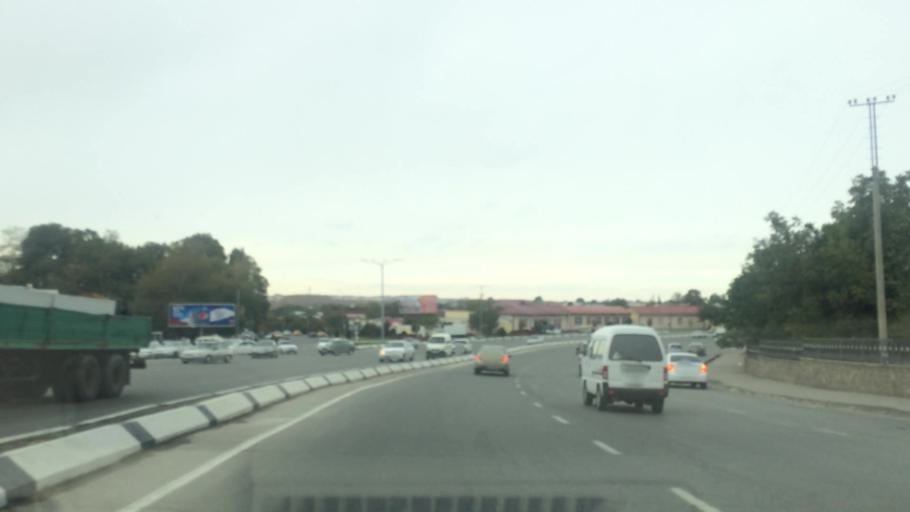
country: UZ
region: Samarqand
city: Samarqand
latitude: 39.6761
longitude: 67.0086
